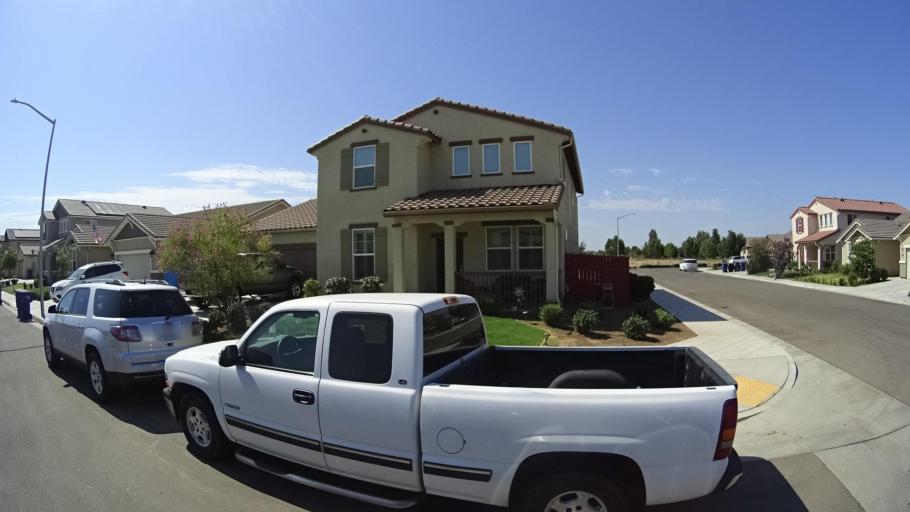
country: US
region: California
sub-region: Fresno County
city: Sunnyside
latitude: 36.7709
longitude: -119.6575
